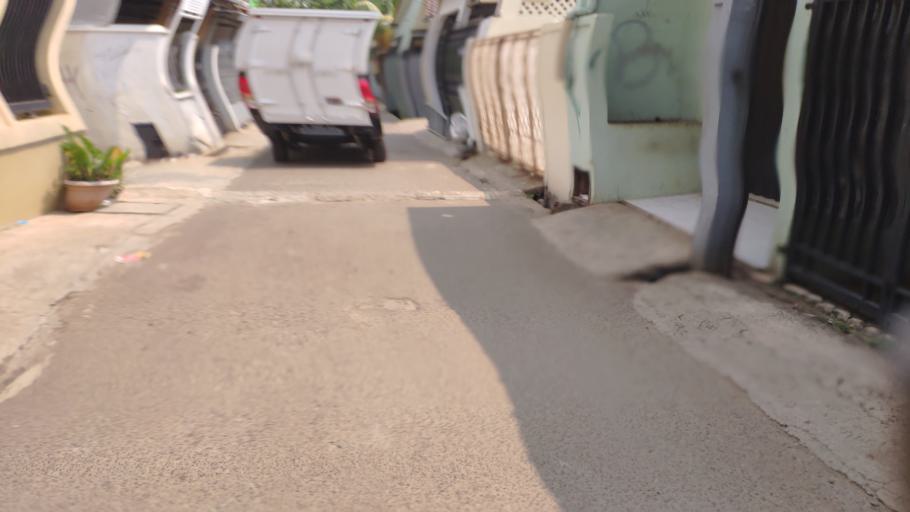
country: ID
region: West Java
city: Pamulang
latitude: -6.3416
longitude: 106.7943
